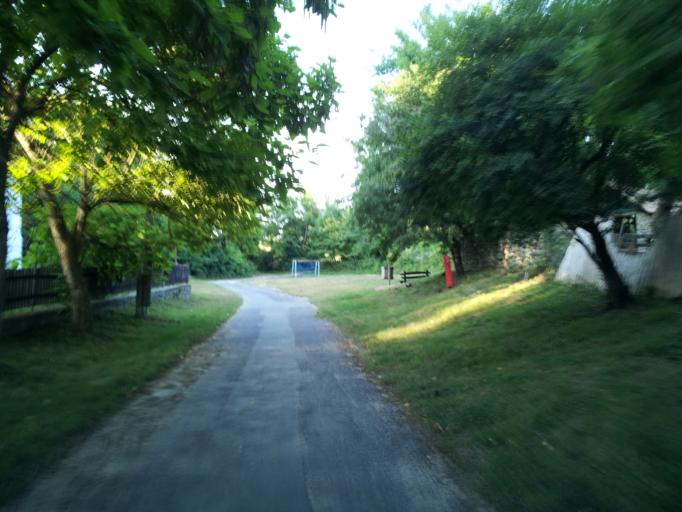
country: HU
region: Veszprem
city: Zanka
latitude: 46.9566
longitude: 17.6083
